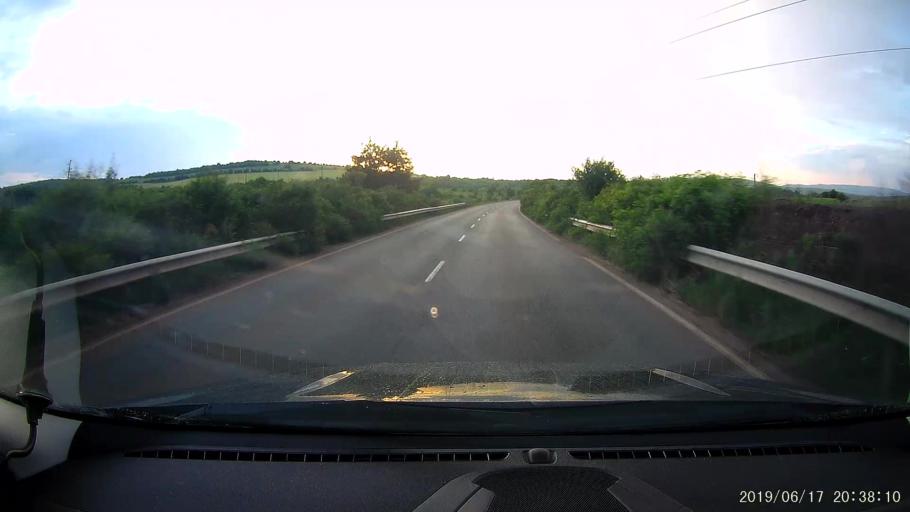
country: BG
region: Sofiya
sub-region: Obshtina Slivnitsa
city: Slivnitsa
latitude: 42.8690
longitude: 23.0211
